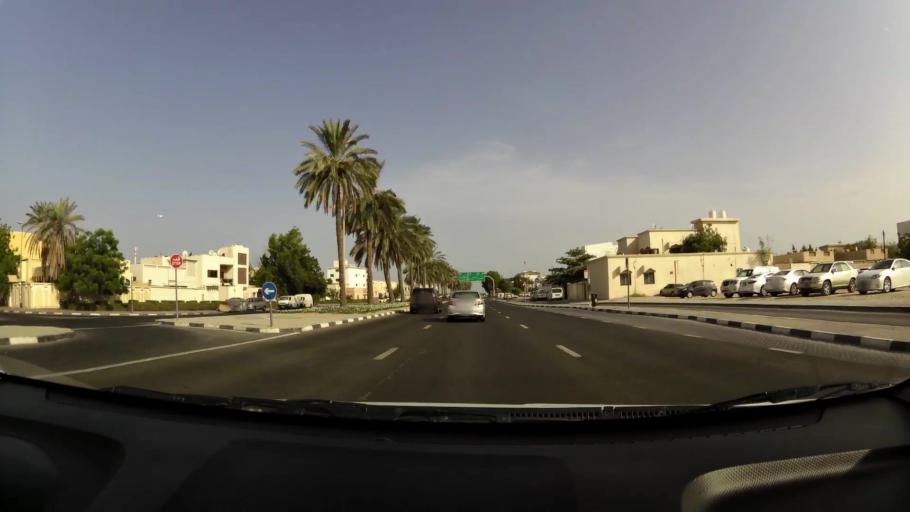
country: AE
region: Ash Shariqah
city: Sharjah
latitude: 25.2904
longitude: 55.3304
